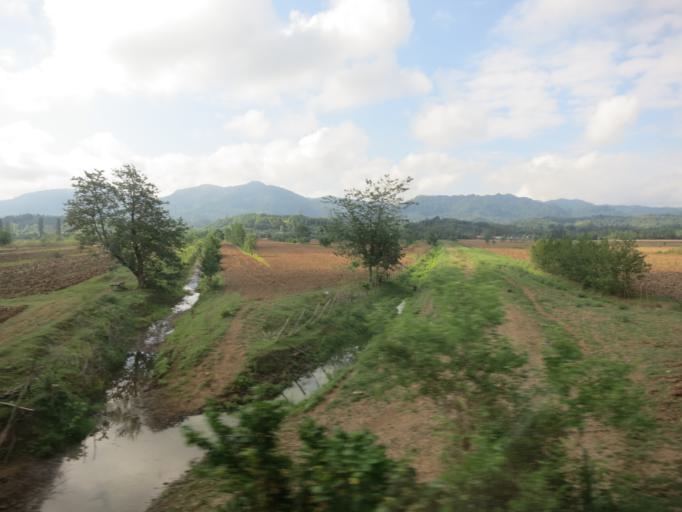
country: GE
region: Guria
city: Lanchkhuti
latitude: 42.0947
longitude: 42.0021
